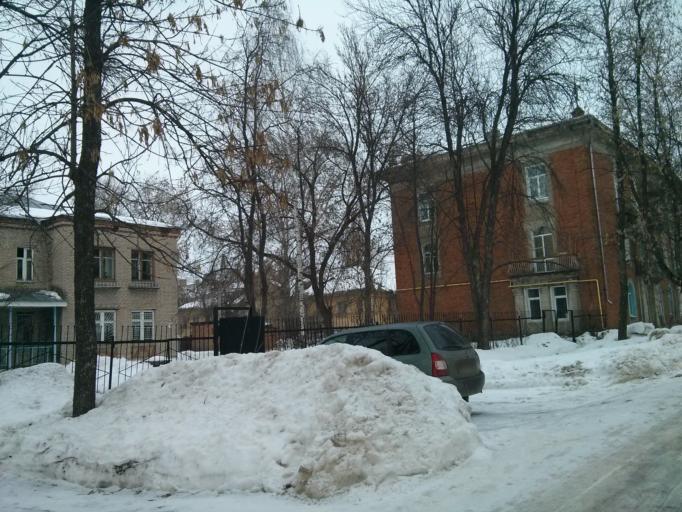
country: RU
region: Vladimir
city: Murom
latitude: 55.5546
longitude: 42.0594
